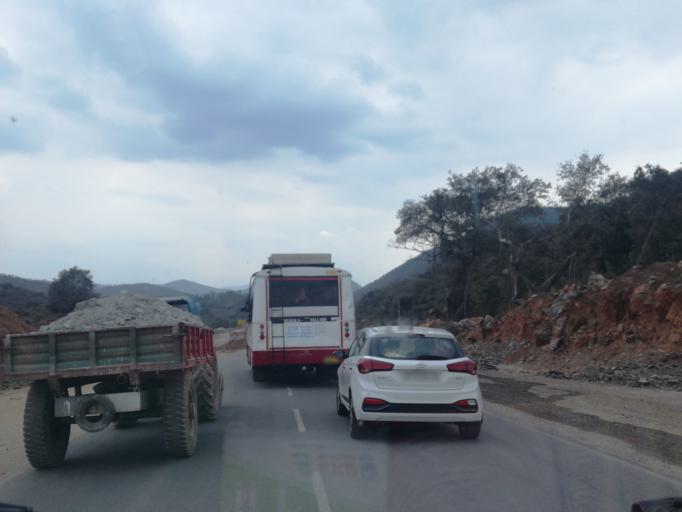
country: IN
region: Andhra Pradesh
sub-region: Chittoor
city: Ramapuram
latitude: 13.0867
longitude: 79.1355
